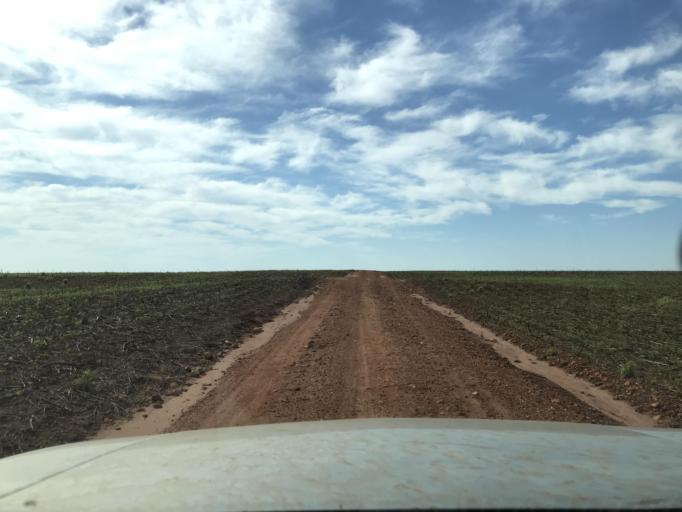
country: BR
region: Parana
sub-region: Palotina
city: Palotina
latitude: -24.1894
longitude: -53.8322
